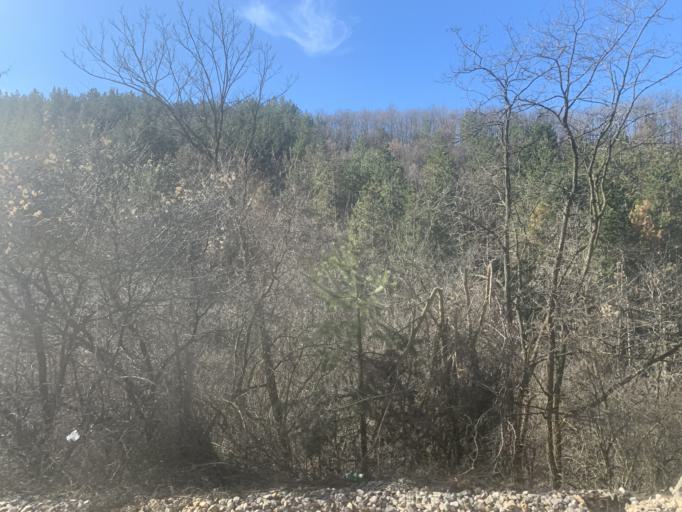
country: BG
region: Sofiya
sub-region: Obshtina Gorna Malina
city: Gorna Malina
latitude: 42.5695
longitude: 23.6722
